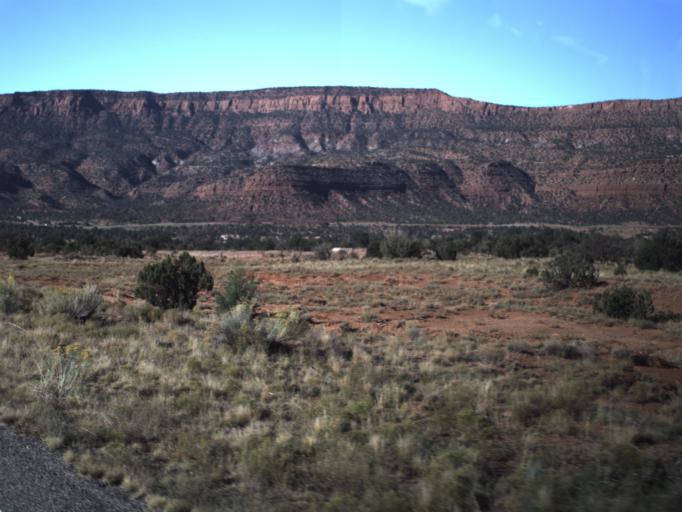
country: US
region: Utah
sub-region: San Juan County
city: Blanding
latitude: 37.6471
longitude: -110.1436
